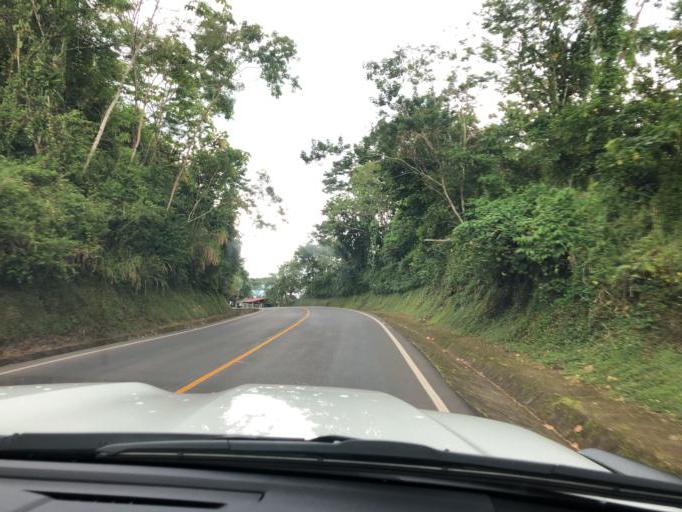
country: NI
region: Chontales
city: Villa Sandino
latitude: 11.9897
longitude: -84.8109
